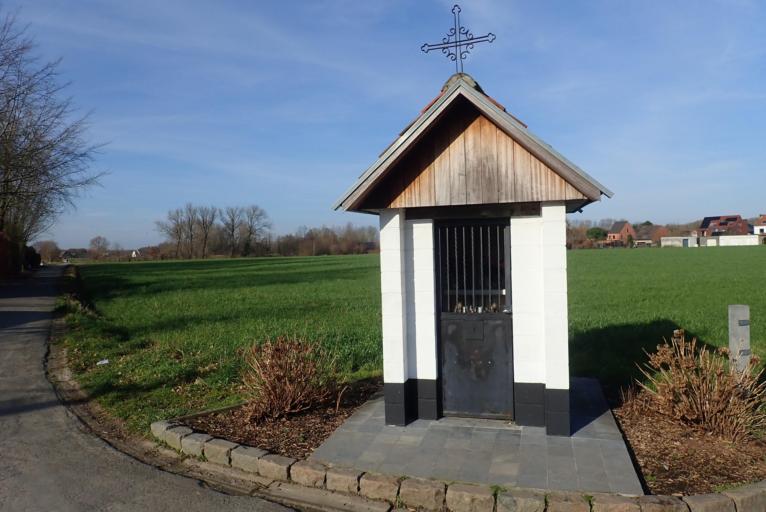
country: BE
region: Flanders
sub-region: Provincie Vlaams-Brabant
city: Opwijk
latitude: 50.9742
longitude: 4.1750
